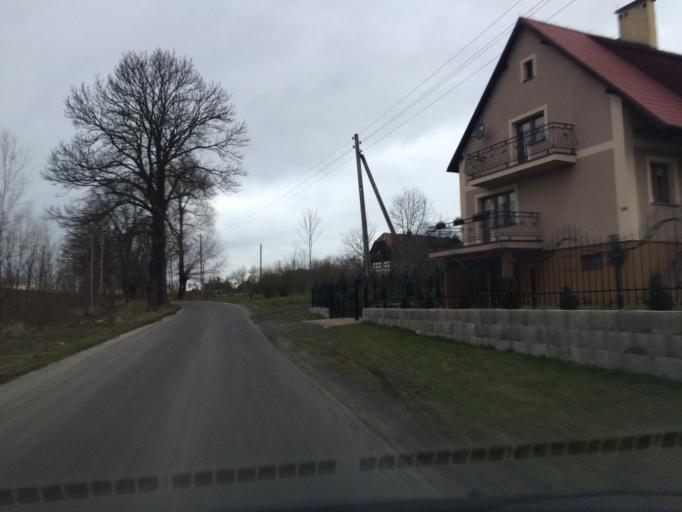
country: PL
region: Lower Silesian Voivodeship
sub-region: Powiat lubanski
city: Pisarzowice
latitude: 51.1648
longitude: 15.2486
